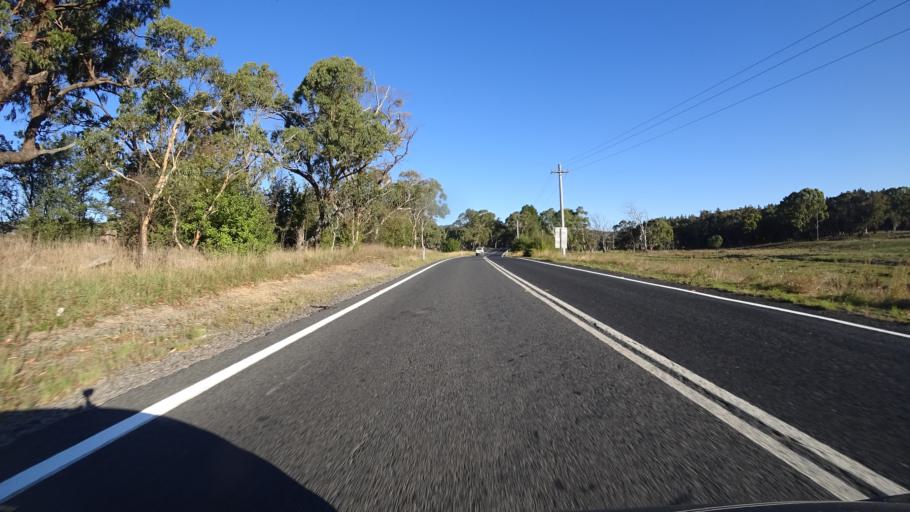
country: AU
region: New South Wales
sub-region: Lithgow
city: Portland
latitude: -33.3119
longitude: 150.0352
